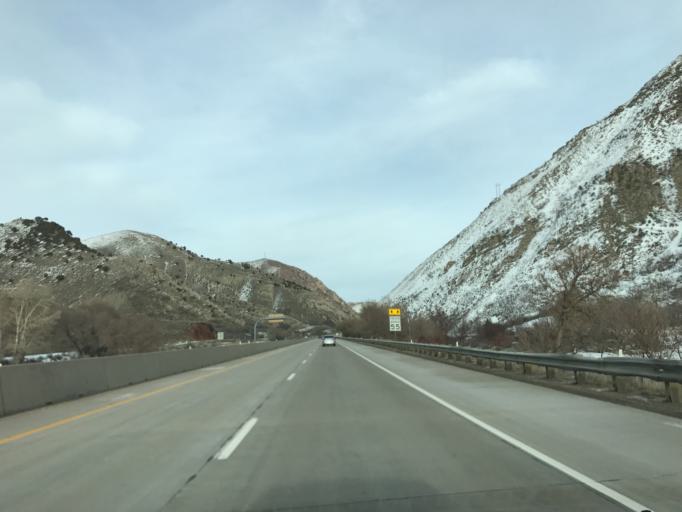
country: US
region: Utah
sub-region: Morgan County
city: Morgan
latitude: 41.0599
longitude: -111.5774
